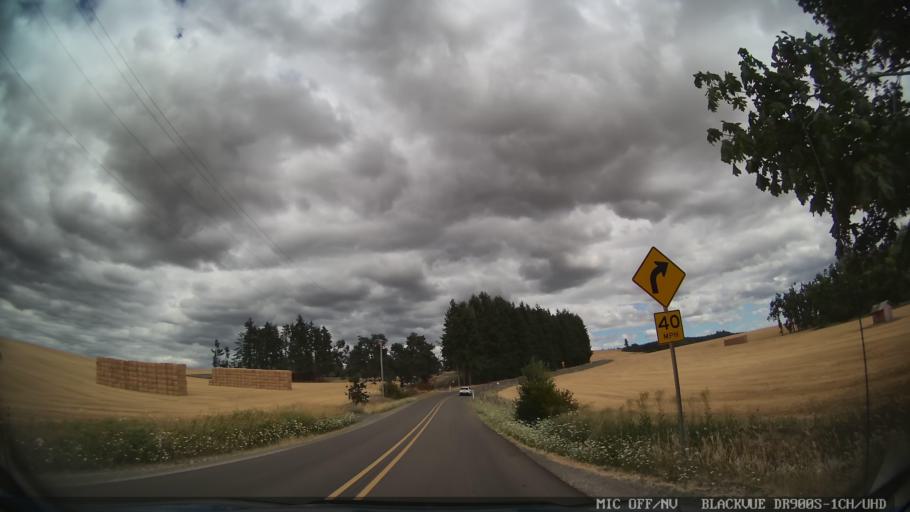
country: US
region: Oregon
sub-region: Marion County
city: Sublimity
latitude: 44.8678
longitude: -122.7481
